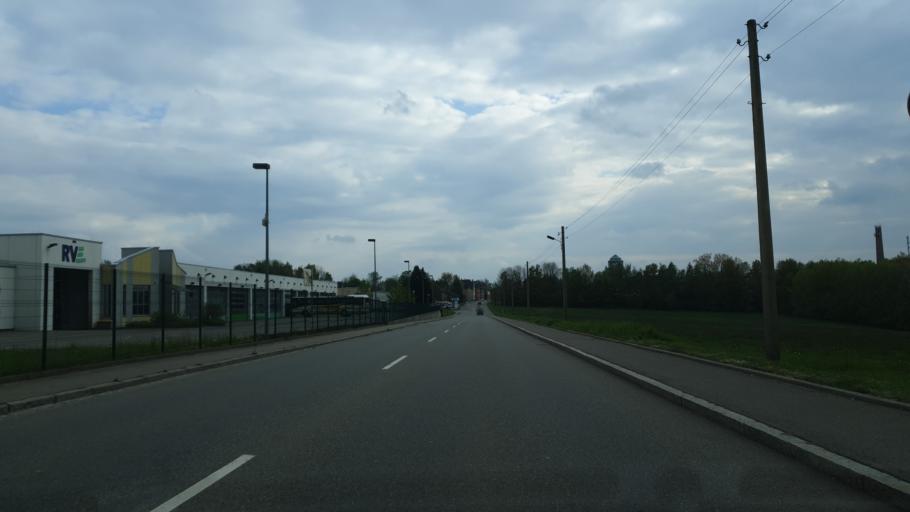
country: DE
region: Saxony
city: Lugau
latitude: 50.7309
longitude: 12.7376
